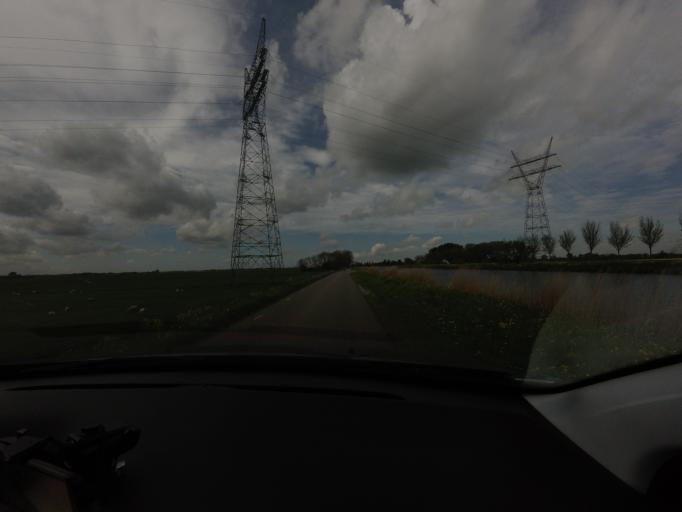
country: NL
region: North Holland
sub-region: Gemeente Beemster
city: Halfweg
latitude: 52.5174
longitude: 4.8988
